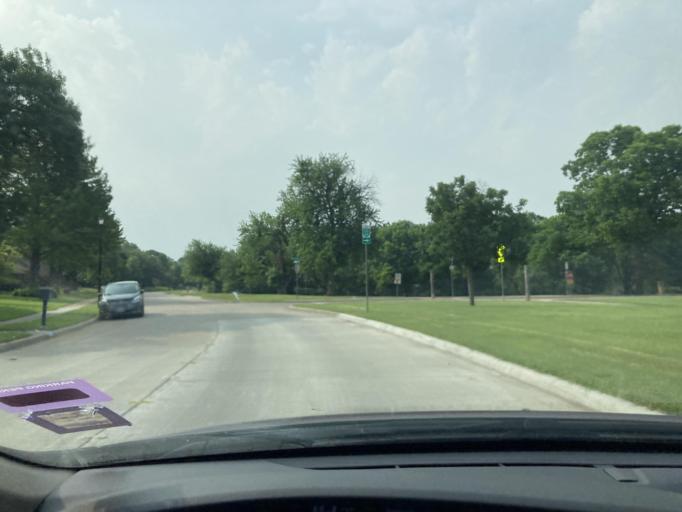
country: US
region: Texas
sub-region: Collin County
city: Plano
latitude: 33.0548
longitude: -96.7292
